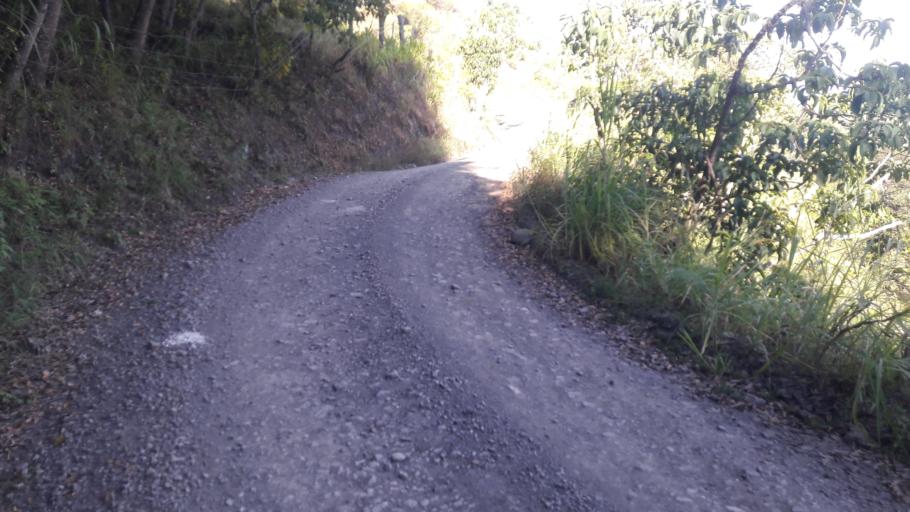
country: CO
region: Cundinamarca
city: Tenza
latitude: 5.0899
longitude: -73.4269
